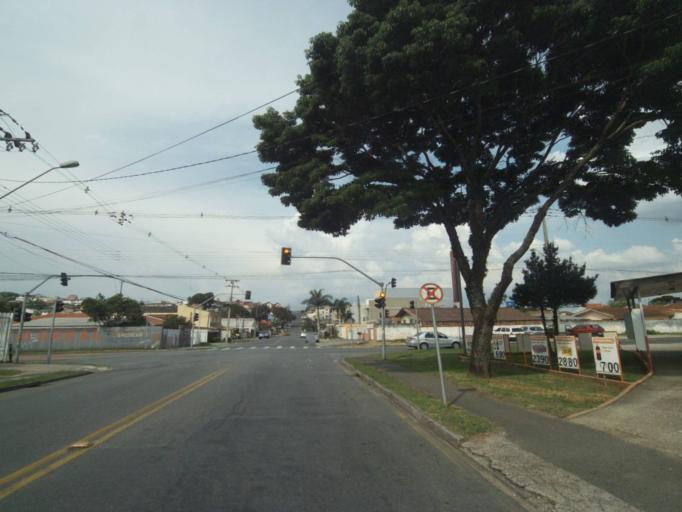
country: BR
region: Parana
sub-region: Pinhais
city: Pinhais
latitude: -25.4094
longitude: -49.2021
